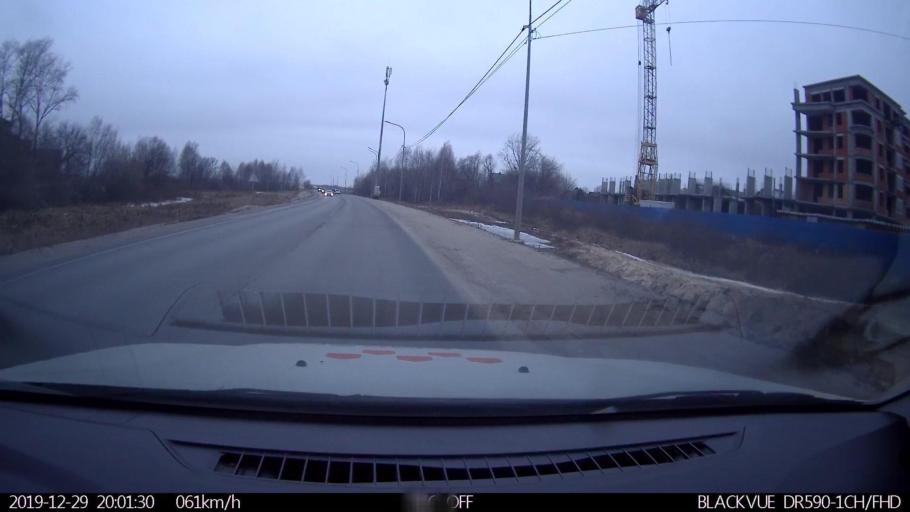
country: RU
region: Nizjnij Novgorod
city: Bor
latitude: 56.3598
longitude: 44.0427
